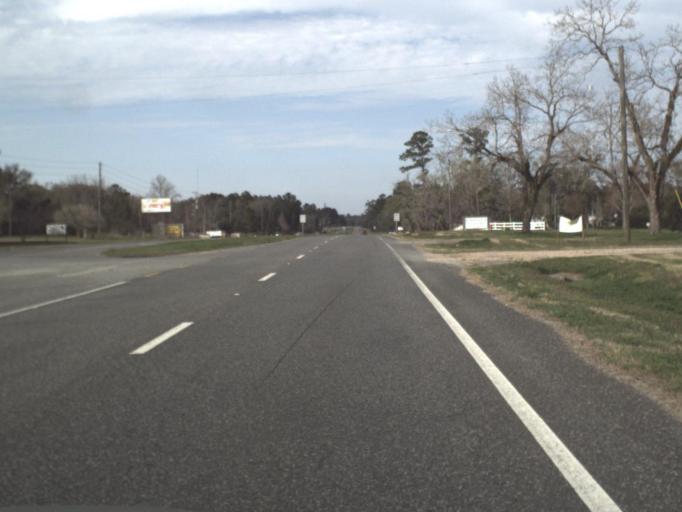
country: US
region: Florida
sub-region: Jefferson County
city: Monticello
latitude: 30.5126
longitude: -83.8758
